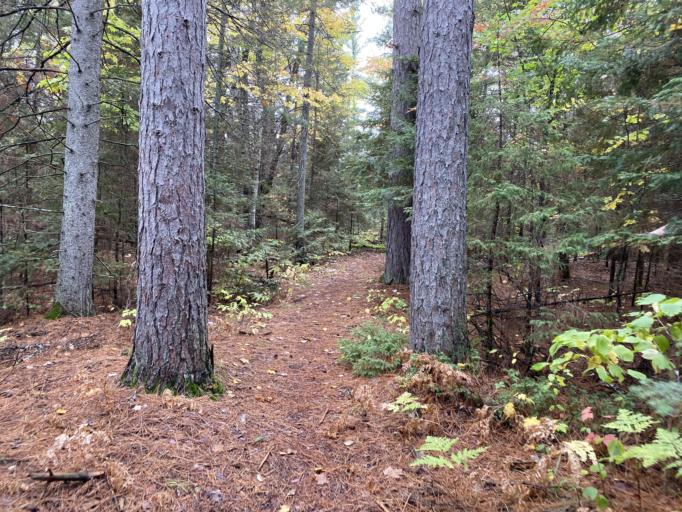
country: US
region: Michigan
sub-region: Marquette County
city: West Ishpeming
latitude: 46.5344
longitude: -88.0025
